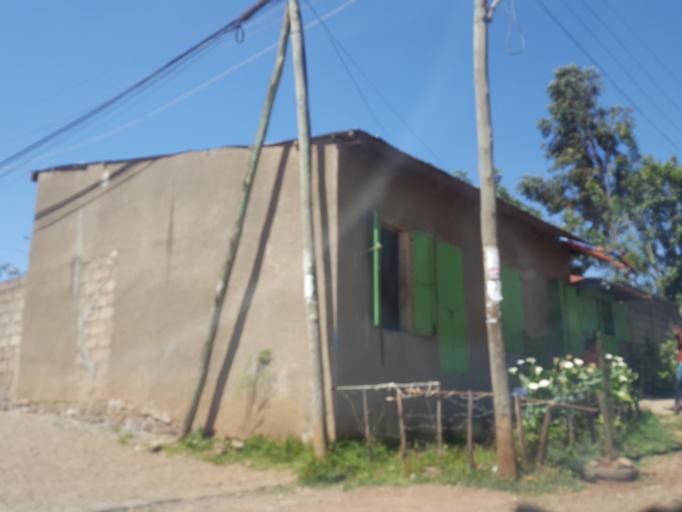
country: ET
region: Adis Abeba
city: Addis Ababa
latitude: 9.0561
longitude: 38.7489
